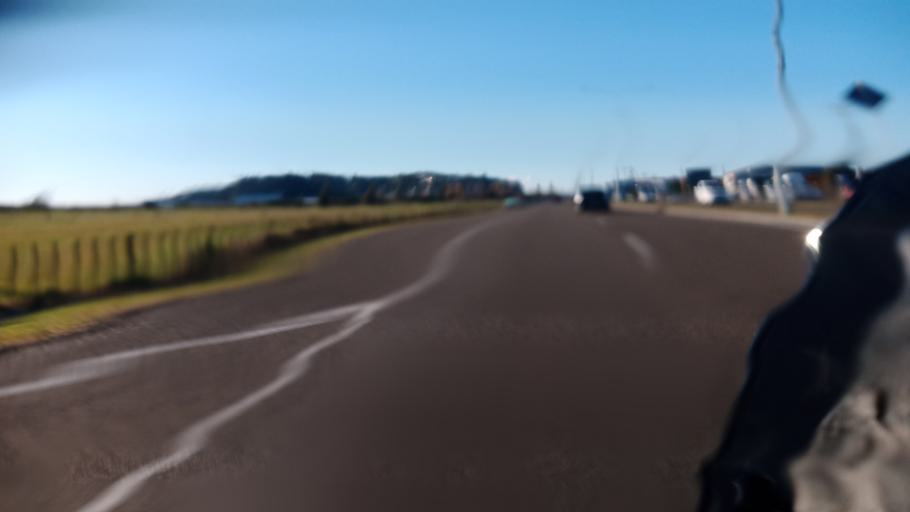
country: NZ
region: Hawke's Bay
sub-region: Napier City
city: Napier
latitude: -39.4964
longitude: 176.8755
